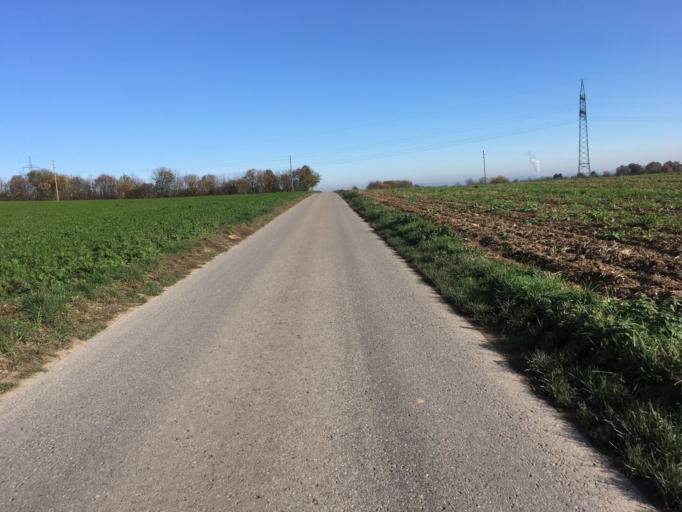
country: DE
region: Baden-Wuerttemberg
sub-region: Regierungsbezirk Stuttgart
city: Pfaffenhofen
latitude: 49.0744
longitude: 8.9767
